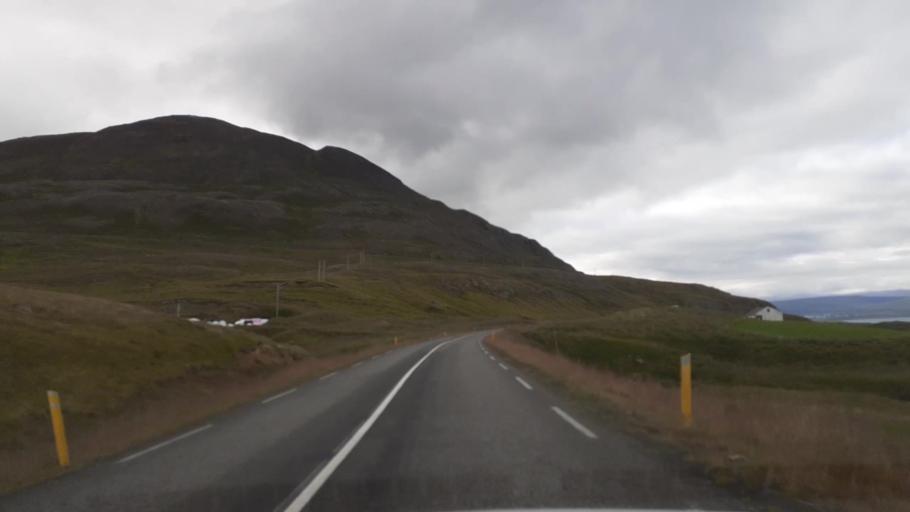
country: IS
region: Northeast
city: Akureyri
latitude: 65.8175
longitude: -18.0489
